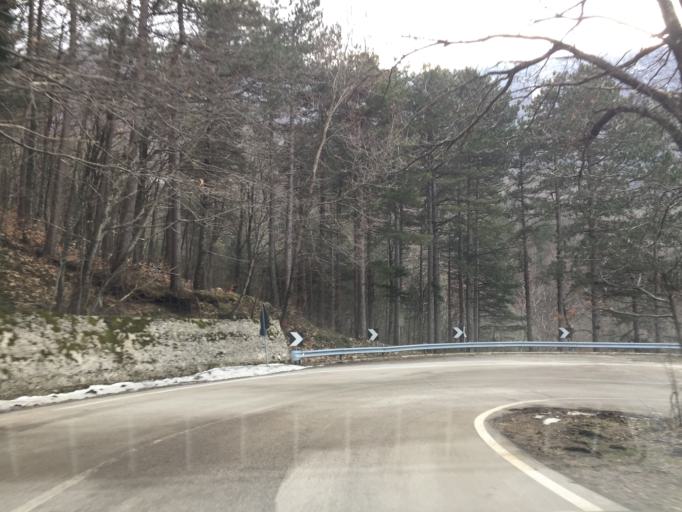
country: IT
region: Molise
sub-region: Provincia di Campobasso
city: San Massimo
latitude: 41.4742
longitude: 14.4093
